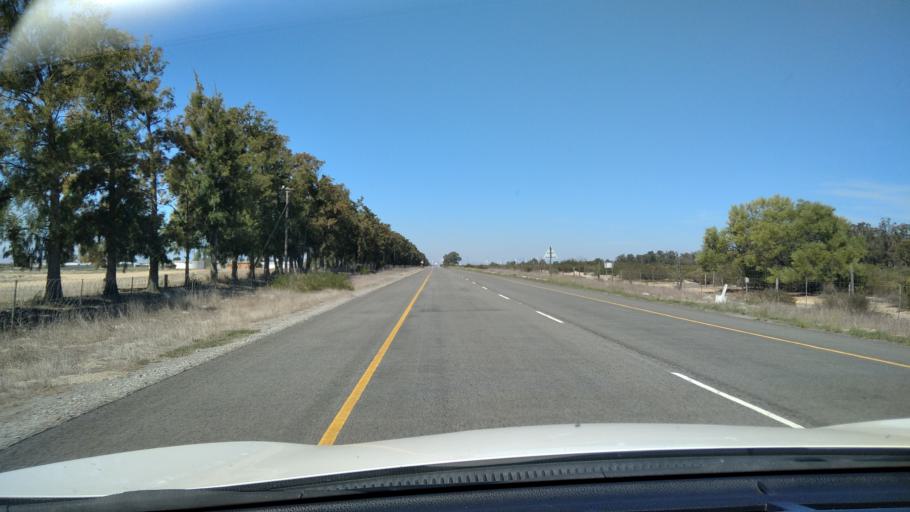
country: ZA
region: Western Cape
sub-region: West Coast District Municipality
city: Vredenburg
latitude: -33.0362
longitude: 18.3001
